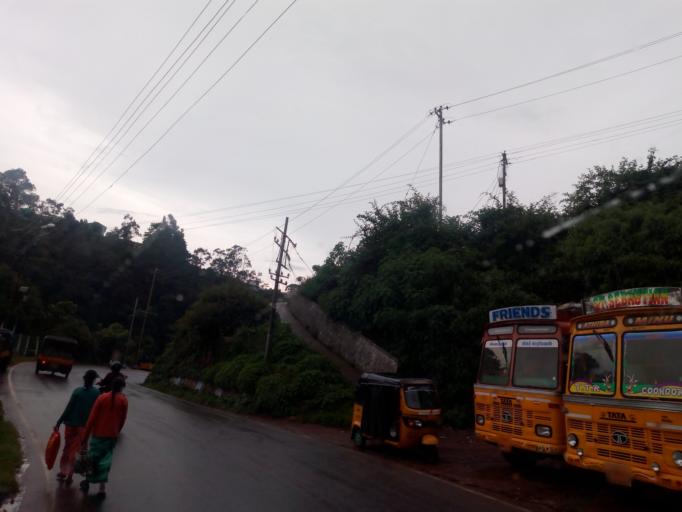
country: IN
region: Tamil Nadu
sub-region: Nilgiri
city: Wellington
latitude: 11.3434
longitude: 76.7966
